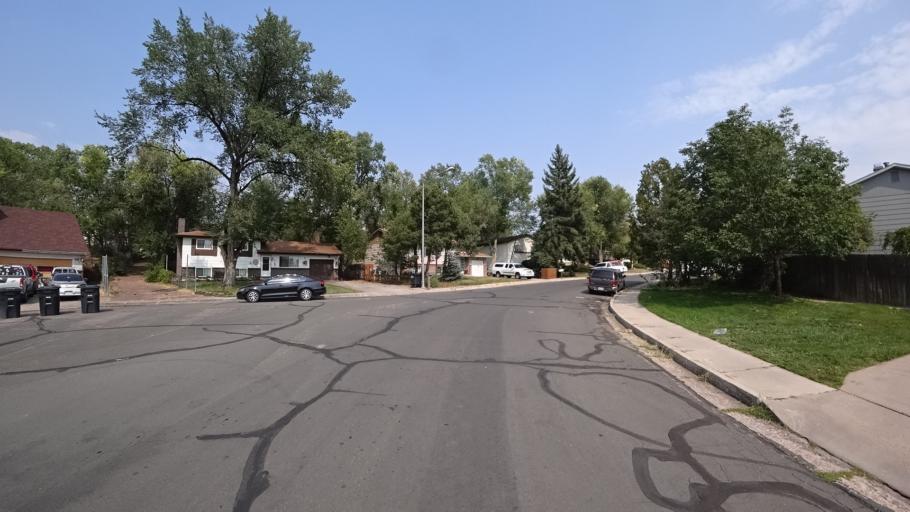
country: US
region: Colorado
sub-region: El Paso County
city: Cimarron Hills
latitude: 38.8314
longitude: -104.7496
